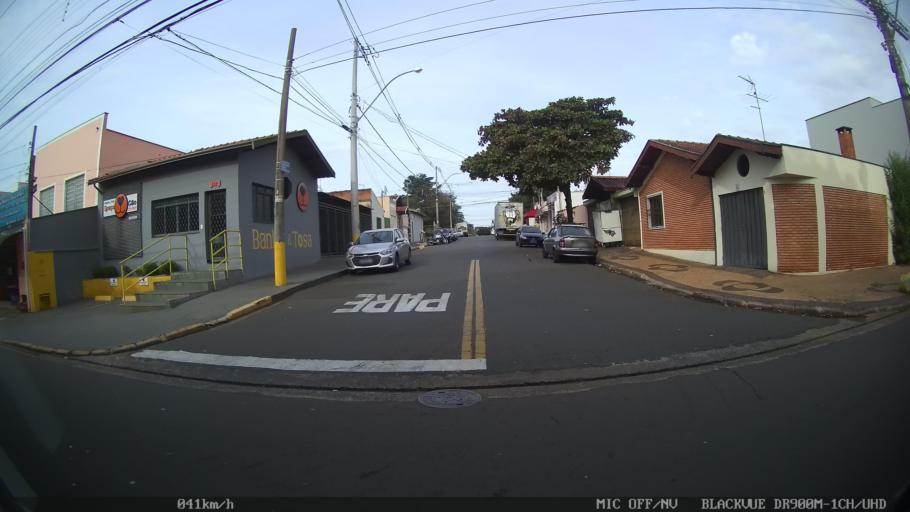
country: BR
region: Sao Paulo
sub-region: Piracicaba
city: Piracicaba
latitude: -22.7367
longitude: -47.6235
